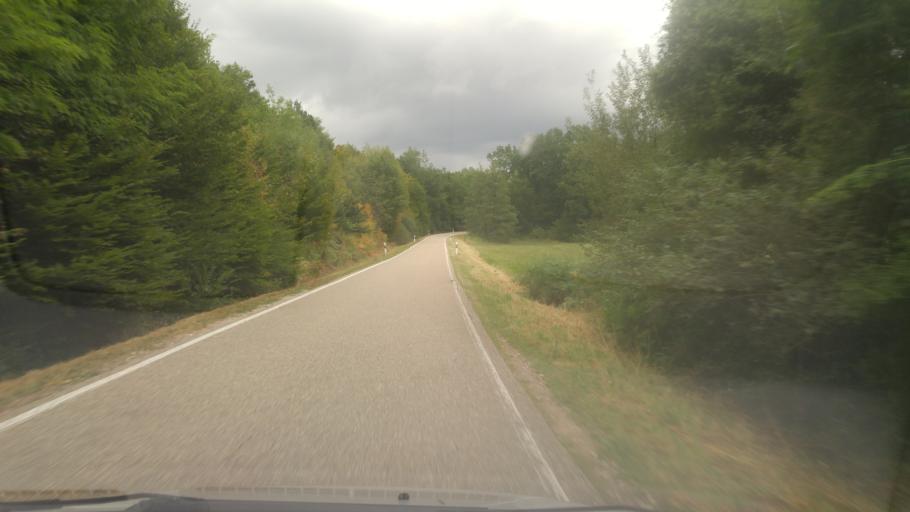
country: DE
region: Rheinland-Pfalz
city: Scheibenhardt
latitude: 48.9871
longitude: 8.1249
